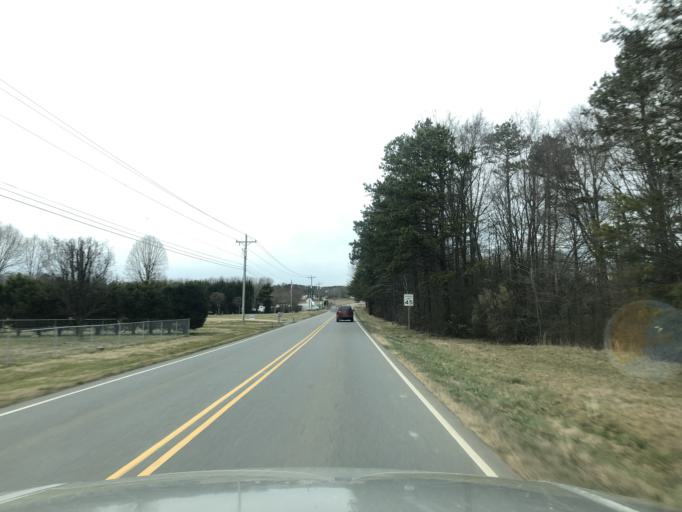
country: US
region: North Carolina
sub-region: Cleveland County
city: Shelby
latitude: 35.3322
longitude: -81.4994
